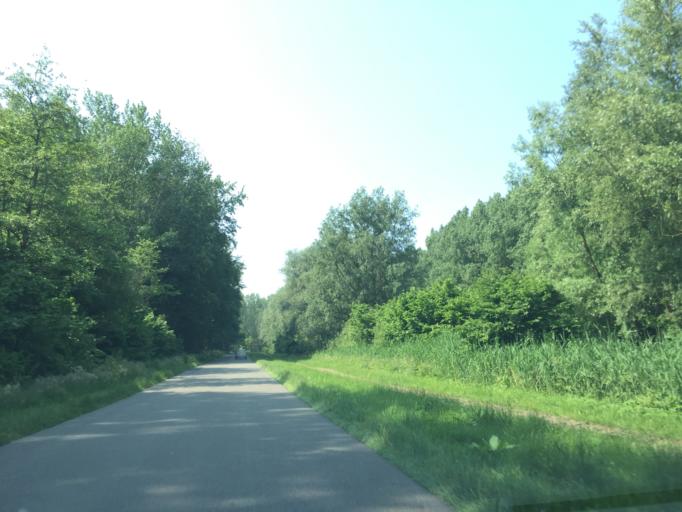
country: NL
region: South Holland
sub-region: Gemeente Voorschoten
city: Voorschoten
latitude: 52.1236
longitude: 4.4718
